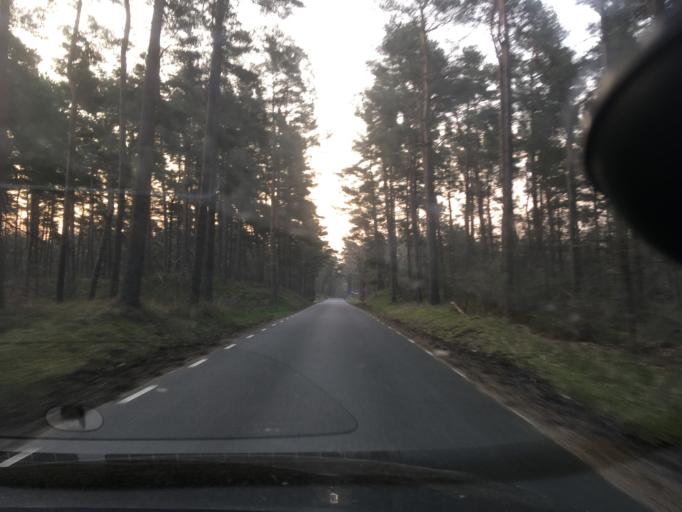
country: SE
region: Skane
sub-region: Simrishamns Kommun
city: Simrishamn
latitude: 55.3914
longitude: 14.1859
